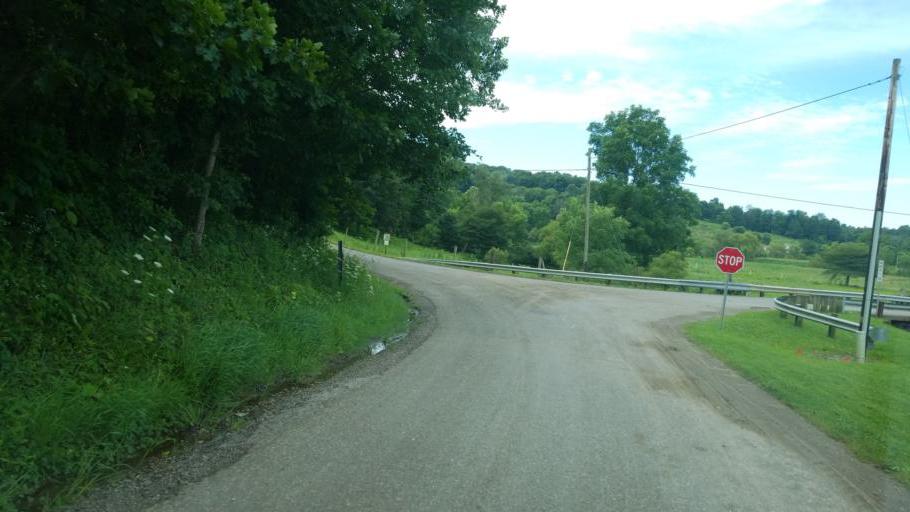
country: US
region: Ohio
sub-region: Holmes County
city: Millersburg
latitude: 40.4847
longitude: -81.8568
